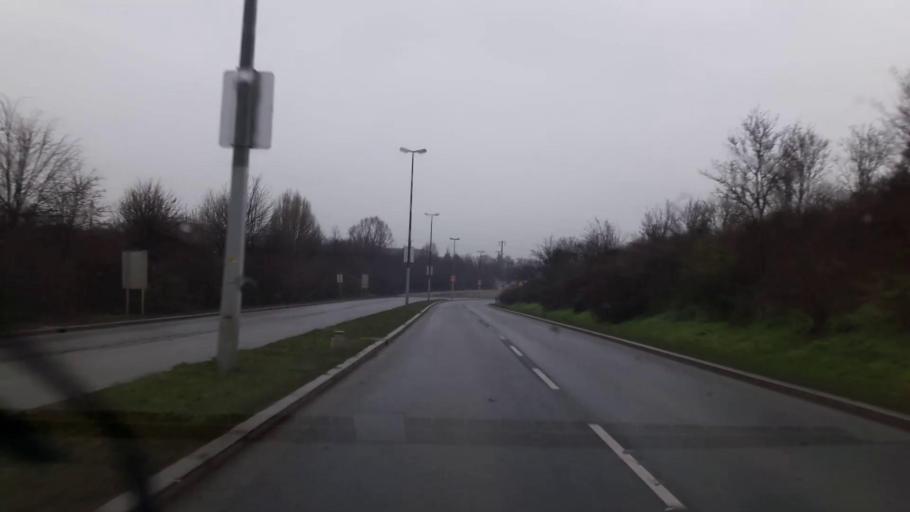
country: AT
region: Lower Austria
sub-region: Politischer Bezirk Wien-Umgebung
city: Gerasdorf bei Wien
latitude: 48.2707
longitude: 16.4756
